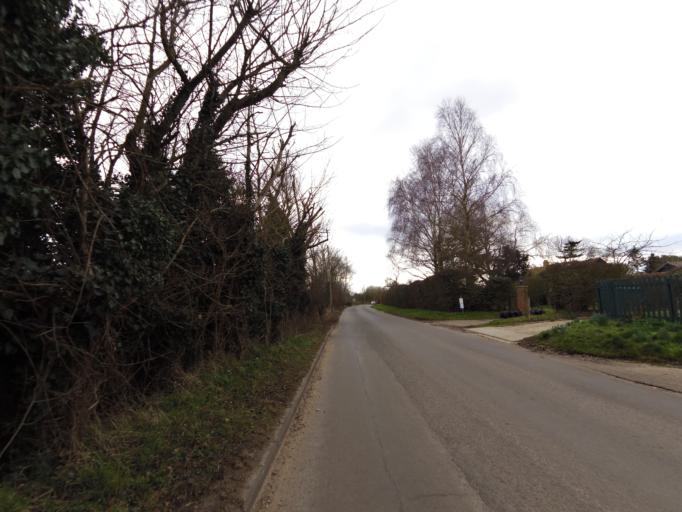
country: GB
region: England
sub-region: Suffolk
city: Woodbridge
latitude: 52.0373
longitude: 1.3142
